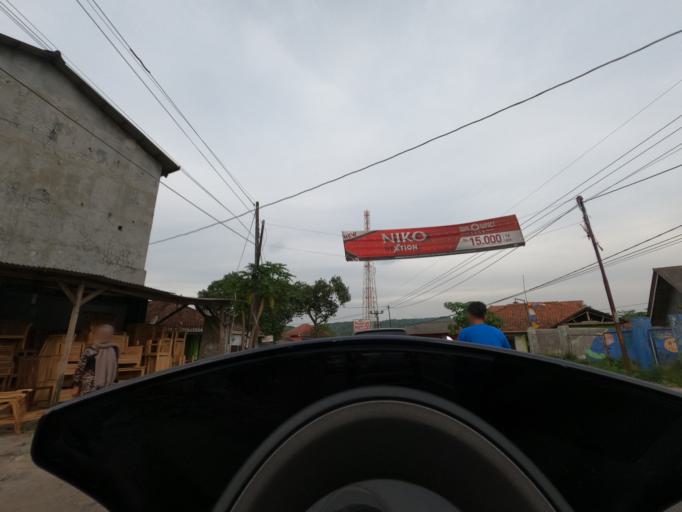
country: ID
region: West Java
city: Lembang
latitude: -6.6567
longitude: 107.7144
